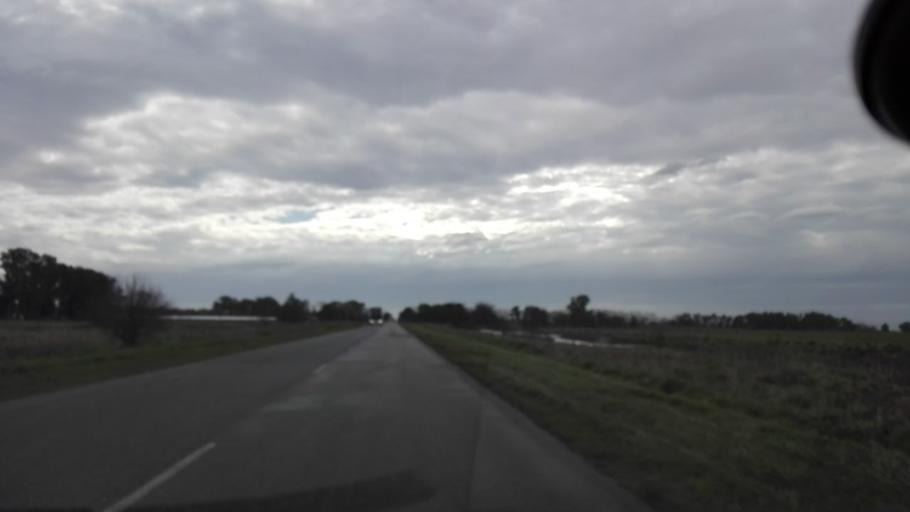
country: AR
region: Buenos Aires
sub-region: Partido de Las Flores
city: Las Flores
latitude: -36.2282
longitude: -59.0446
